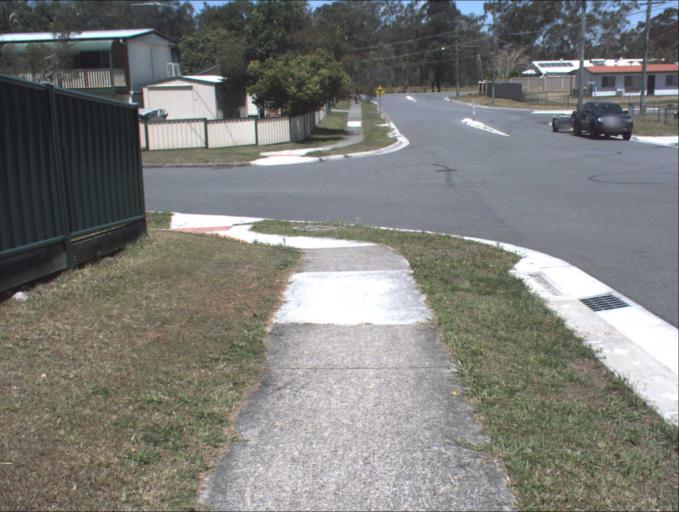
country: AU
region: Queensland
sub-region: Logan
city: Logan City
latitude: -27.6633
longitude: 153.1048
